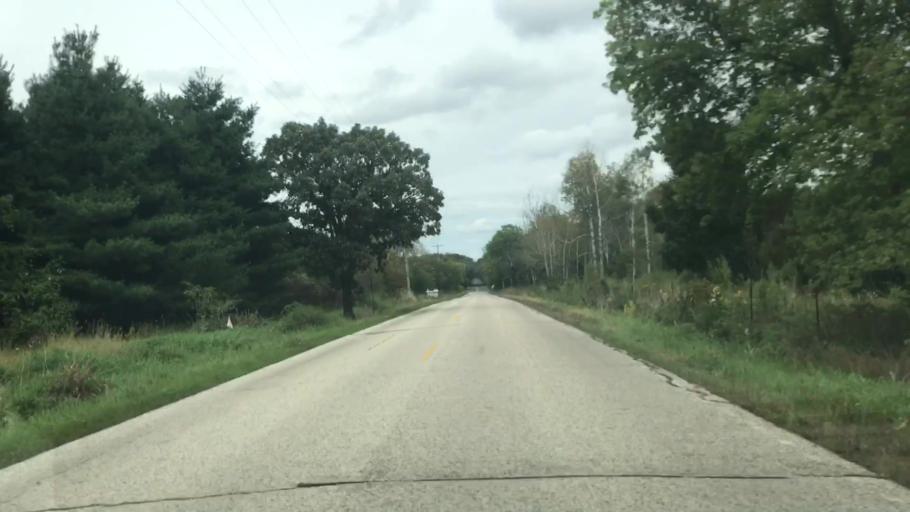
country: US
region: Wisconsin
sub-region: Waukesha County
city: North Prairie
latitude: 42.9151
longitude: -88.4282
